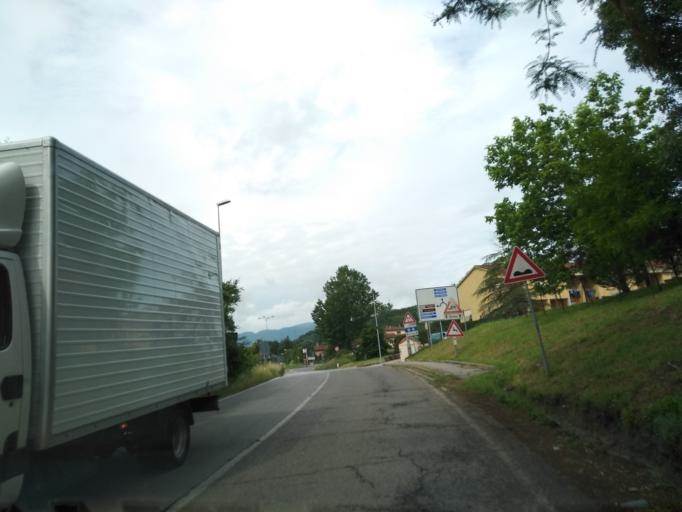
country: IT
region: Tuscany
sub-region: Province of Arezzo
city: Vacchereccia
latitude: 43.5792
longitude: 11.5093
